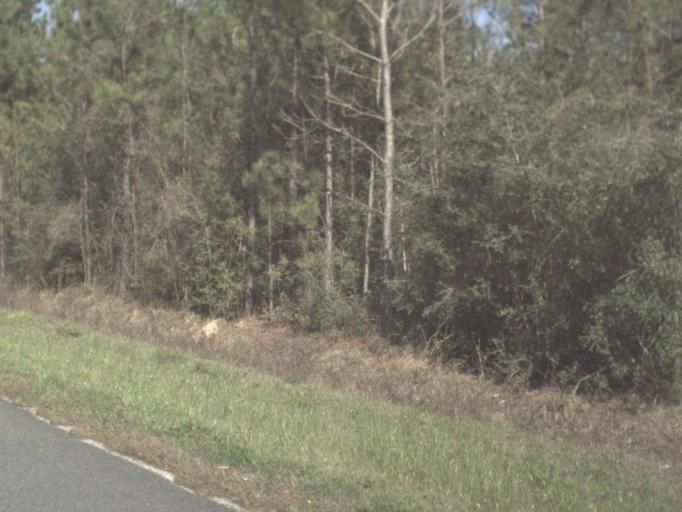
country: US
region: Florida
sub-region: Gulf County
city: Wewahitchka
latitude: 30.2058
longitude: -85.2088
